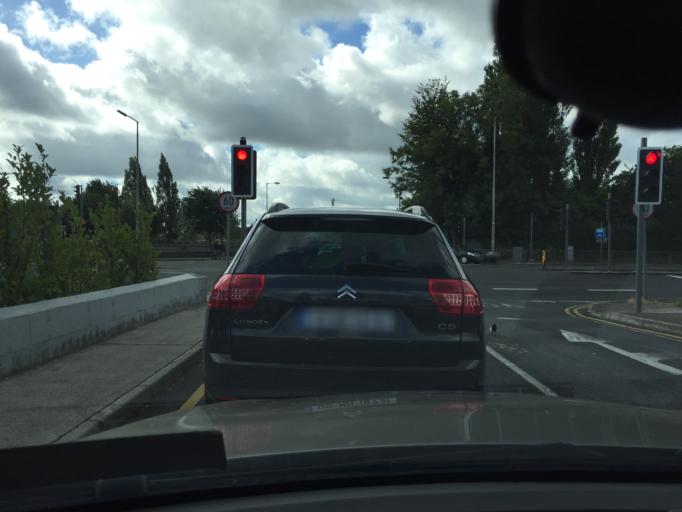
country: IE
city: Palmerstown
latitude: 53.3542
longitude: -6.3676
